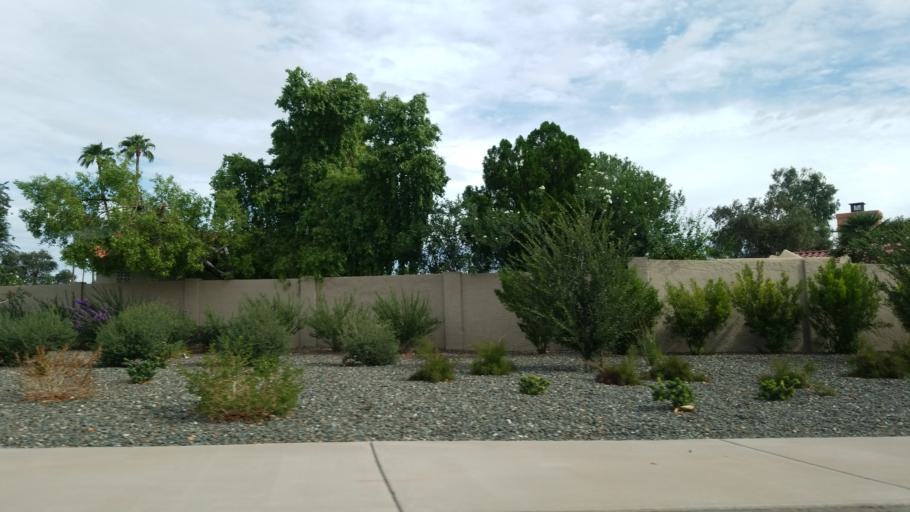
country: US
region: Arizona
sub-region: Maricopa County
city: Paradise Valley
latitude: 33.5755
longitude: -111.9036
